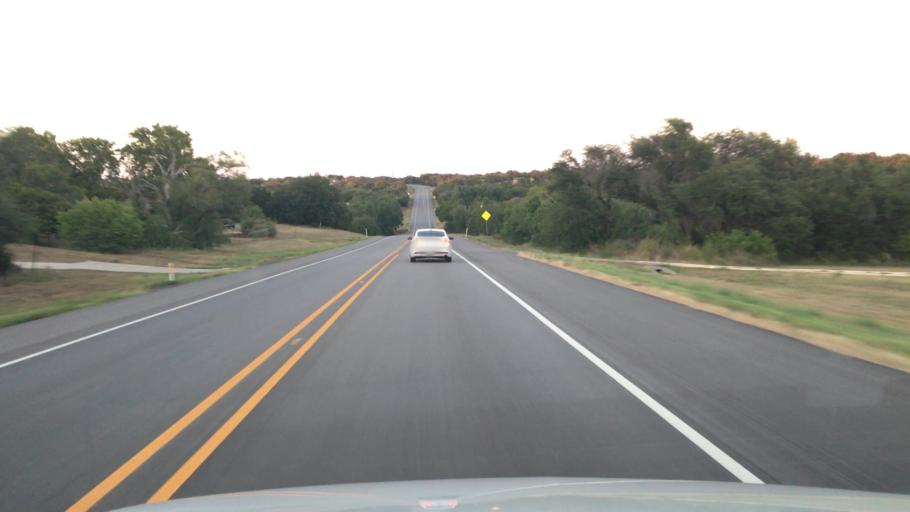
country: US
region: Texas
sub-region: Somervell County
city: Glen Rose
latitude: 32.1921
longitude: -97.8219
